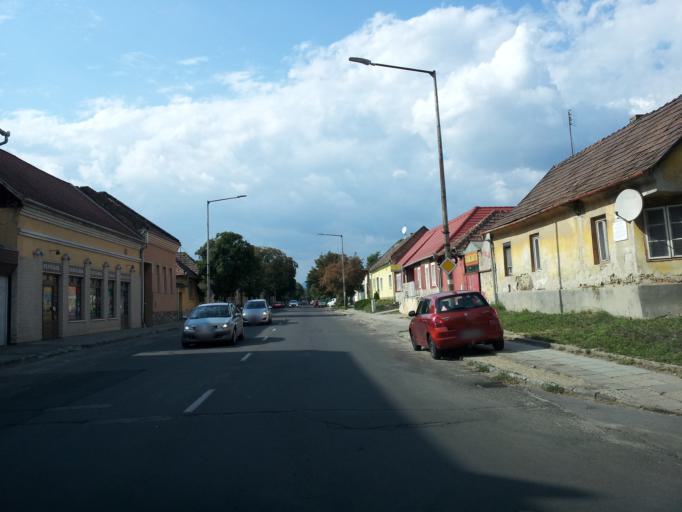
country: HU
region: Pest
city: Vac
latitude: 47.7848
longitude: 19.1229
